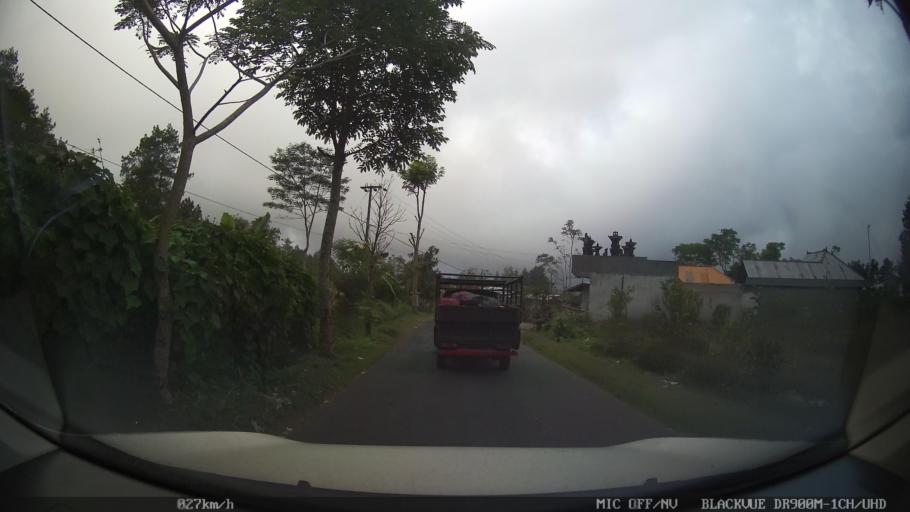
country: ID
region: Bali
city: Banjar Kedisan
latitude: -8.2704
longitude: 115.3307
